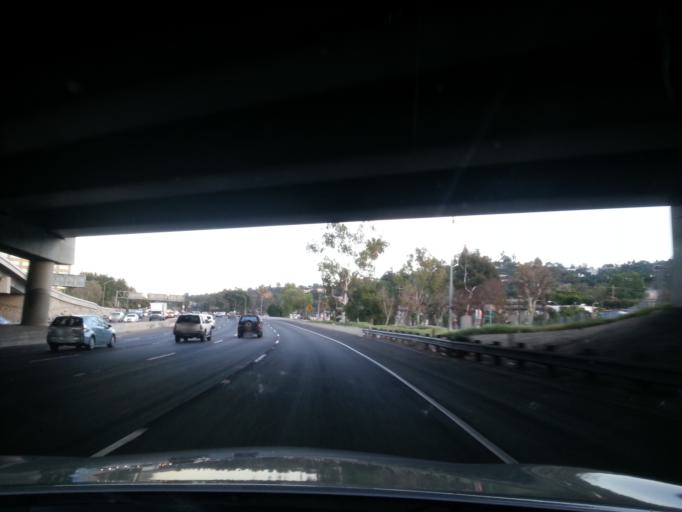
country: US
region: California
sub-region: Los Angeles County
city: Universal City
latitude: 34.1401
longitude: -118.3660
